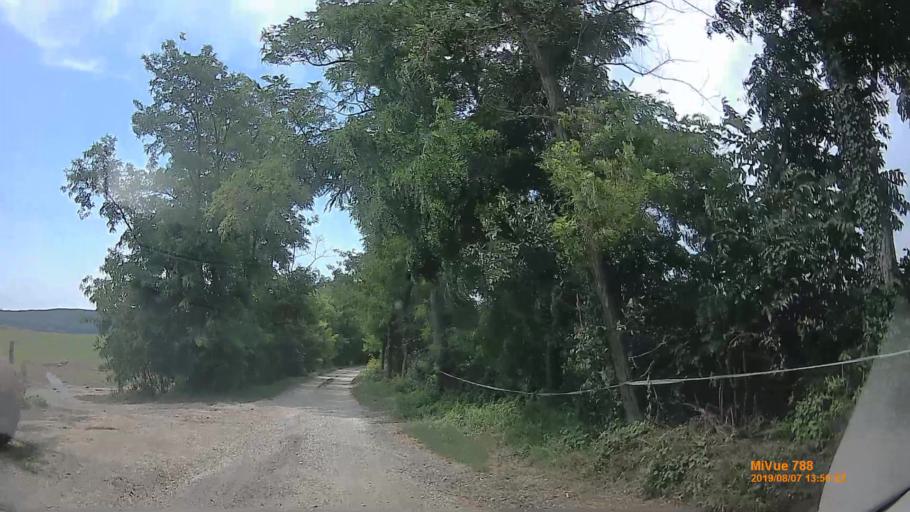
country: HU
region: Zala
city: Cserszegtomaj
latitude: 46.8938
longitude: 17.1776
